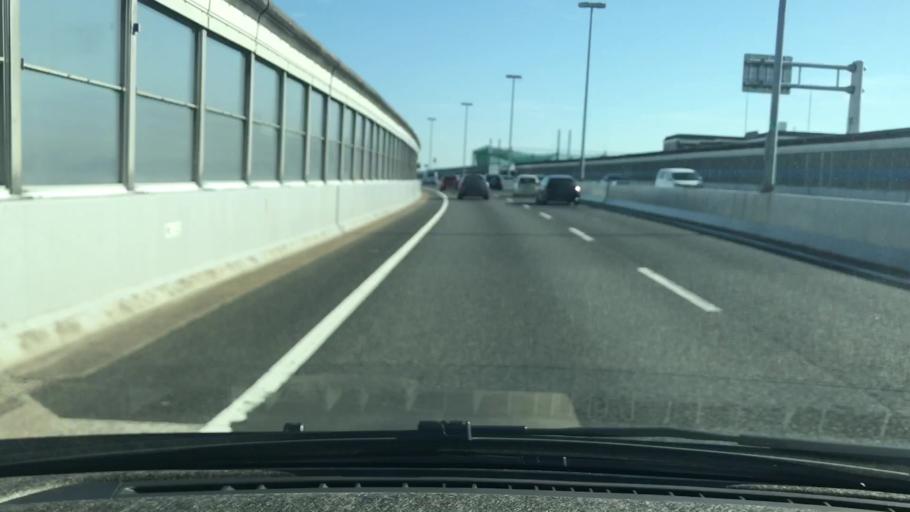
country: JP
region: Hyogo
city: Ashiya
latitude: 34.7112
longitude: 135.2666
